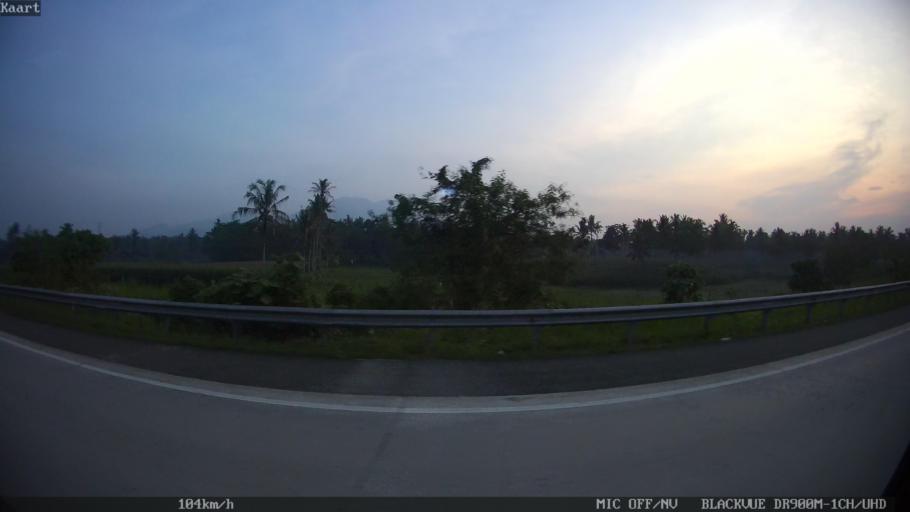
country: ID
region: Lampung
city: Pasuruan
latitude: -5.7143
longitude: 105.6537
